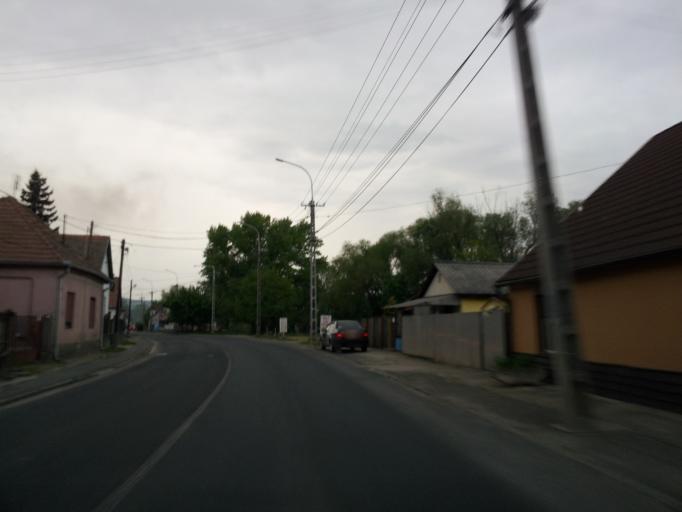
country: HU
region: Pest
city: Dunabogdany
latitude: 47.7968
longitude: 19.0289
